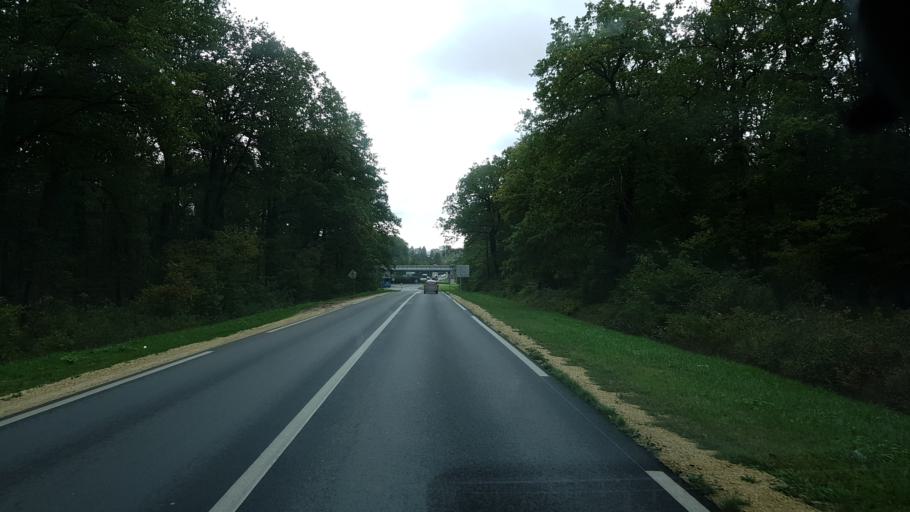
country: FR
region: Centre
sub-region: Departement du Cher
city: Vierzon
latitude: 47.2515
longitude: 2.0603
